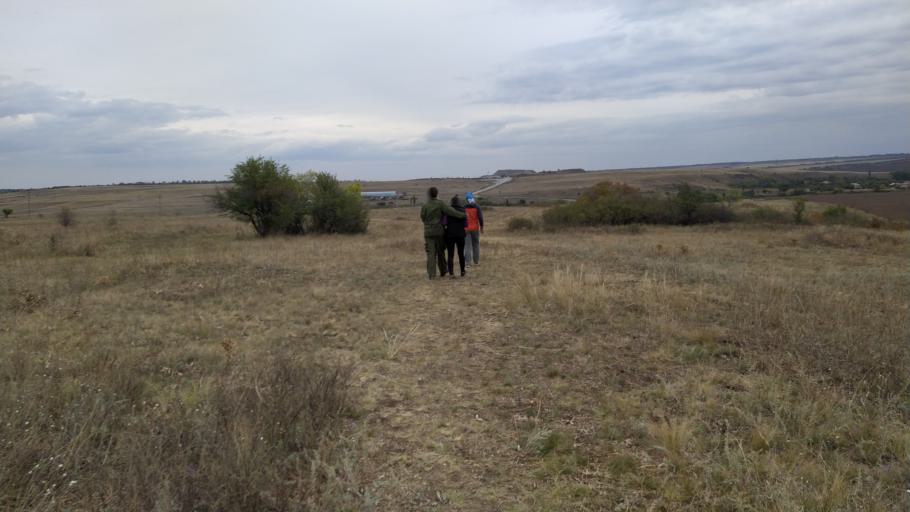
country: RU
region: Rostov
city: Gornyy
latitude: 47.8898
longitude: 40.2414
